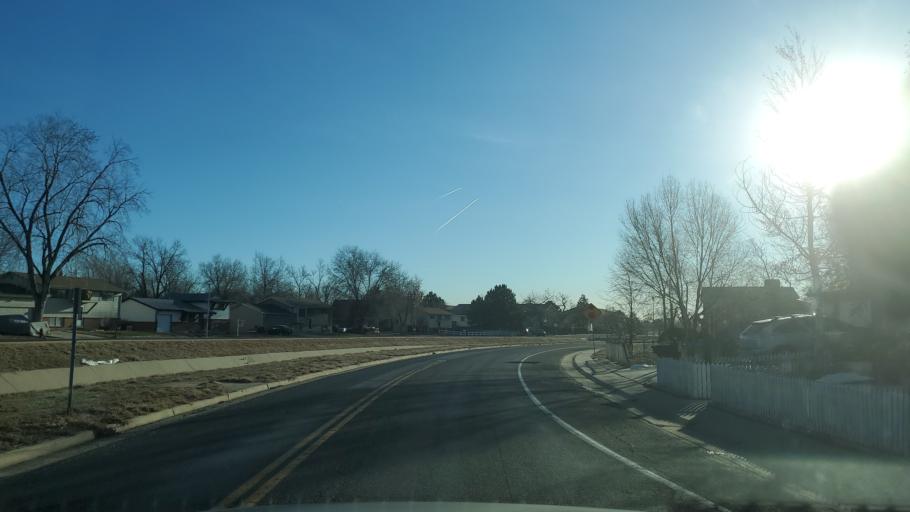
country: US
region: Colorado
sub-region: Adams County
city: Welby
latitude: 39.8441
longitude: -104.9706
